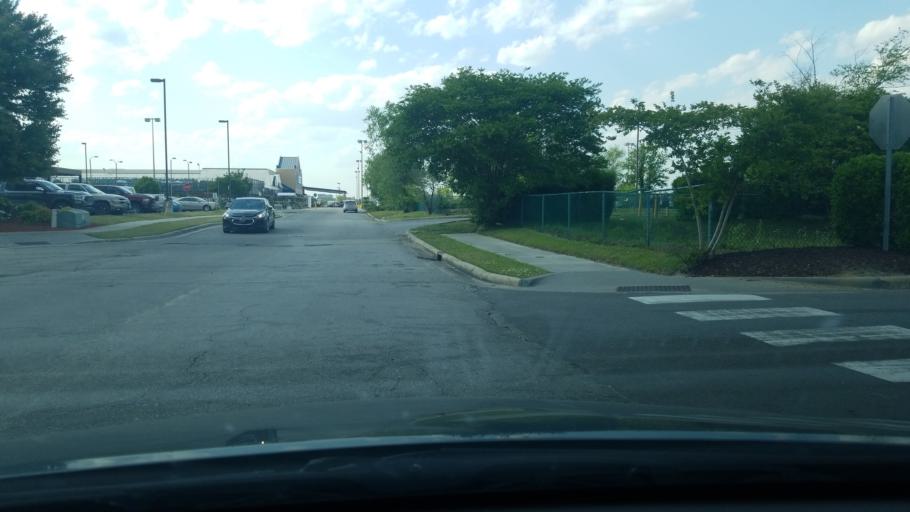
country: US
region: North Carolina
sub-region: Onslow County
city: Pumpkin Center
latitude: 34.7820
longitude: -77.3995
